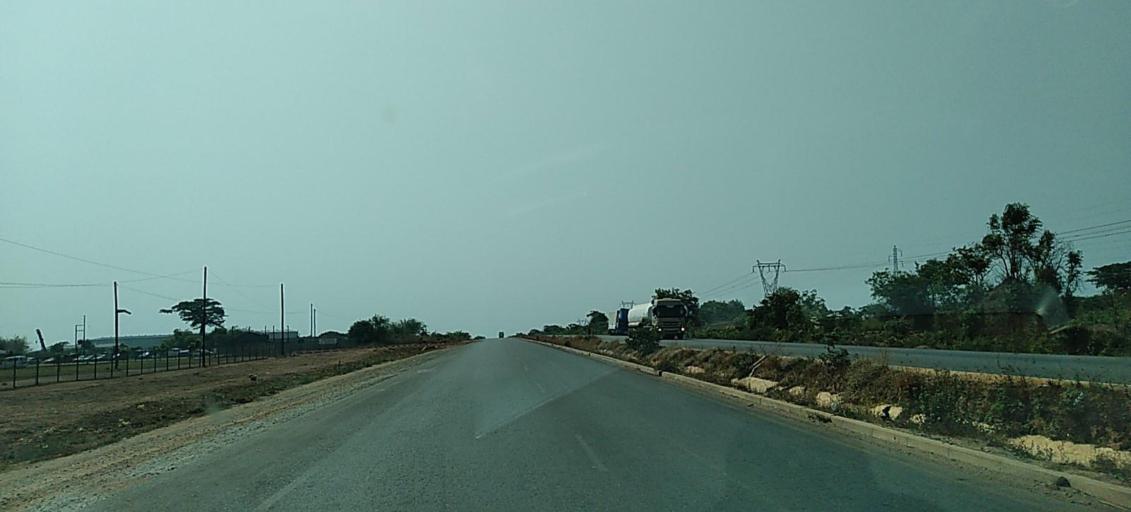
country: ZM
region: Copperbelt
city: Chingola
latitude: -12.5695
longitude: 27.9072
